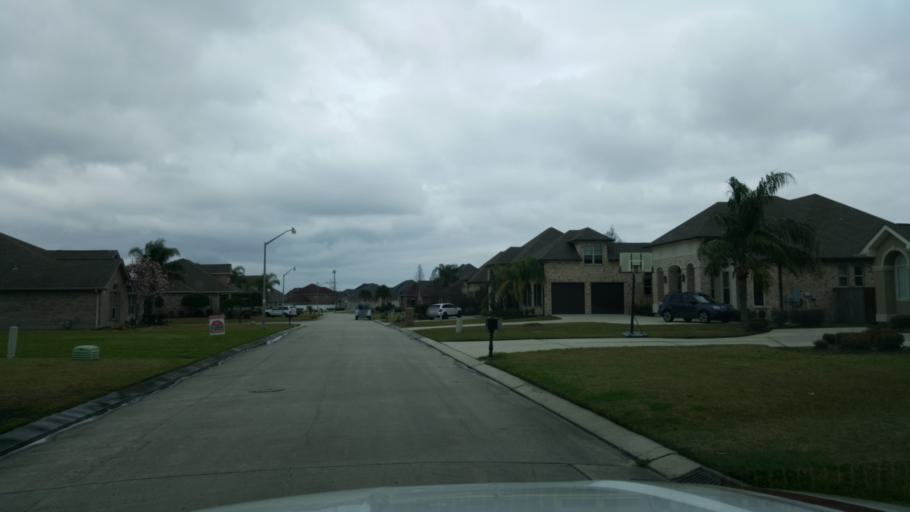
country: US
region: Louisiana
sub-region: Jefferson Parish
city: Woodmere
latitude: 29.8747
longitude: -90.0762
